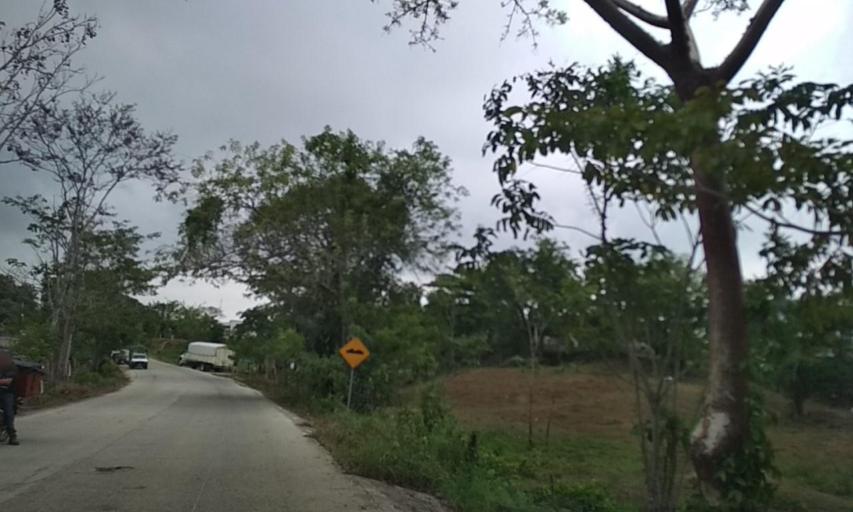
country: MX
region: Tabasco
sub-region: Huimanguillo
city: Francisco Rueda
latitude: 17.6524
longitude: -94.0923
